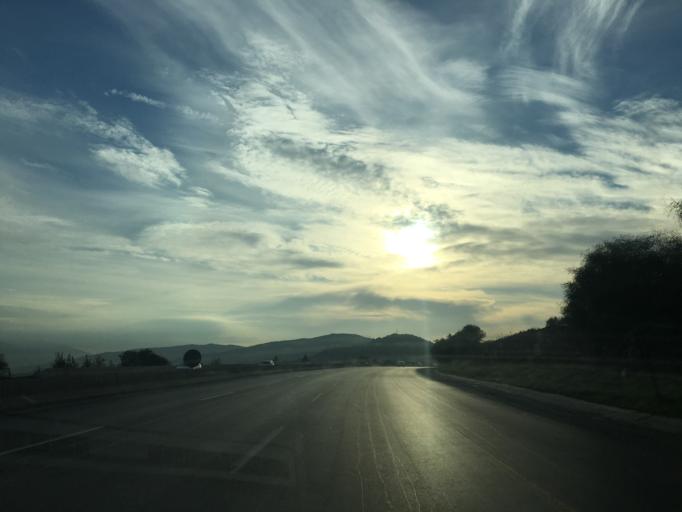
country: DZ
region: Bouira
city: Draa el Mizan
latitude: 36.4718
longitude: 3.7619
